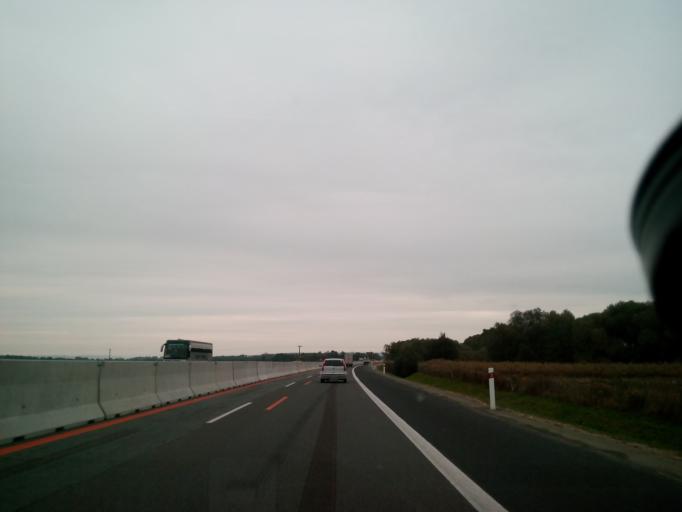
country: SK
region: Kosicky
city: Kosice
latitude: 48.8075
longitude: 21.3095
